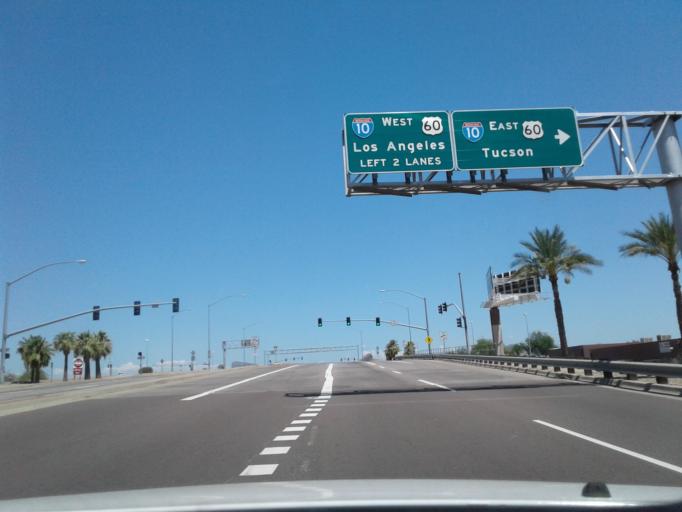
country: US
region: Arizona
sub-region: Maricopa County
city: Guadalupe
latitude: 33.4087
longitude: -111.9953
